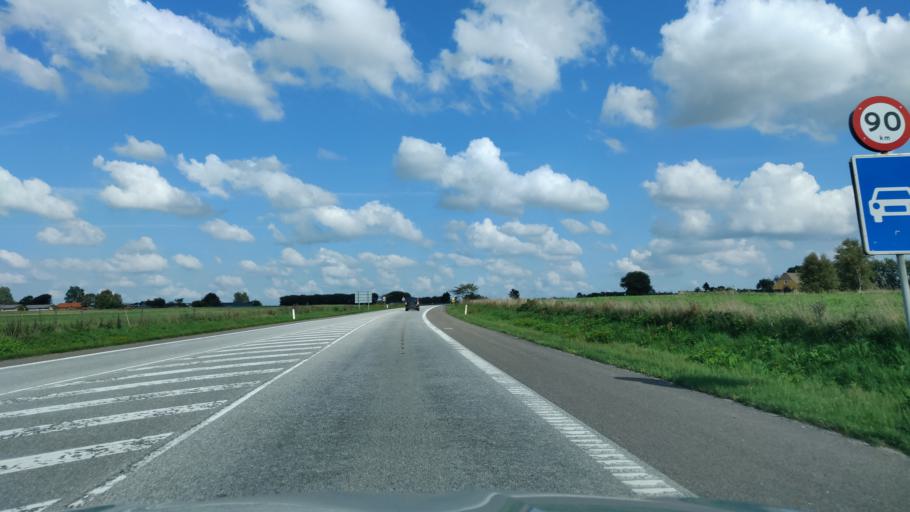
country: DK
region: North Denmark
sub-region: Vesthimmerland Kommune
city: Aars
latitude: 56.8099
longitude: 9.6549
